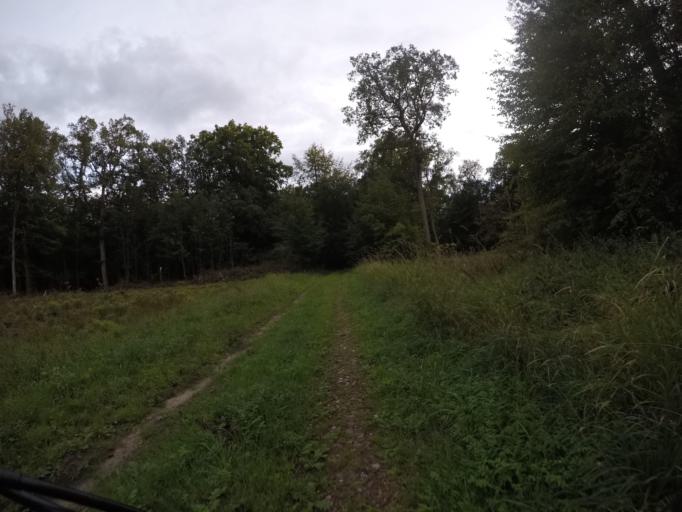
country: DE
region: Lower Saxony
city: Neu Darchau
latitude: 53.2759
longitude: 10.8914
